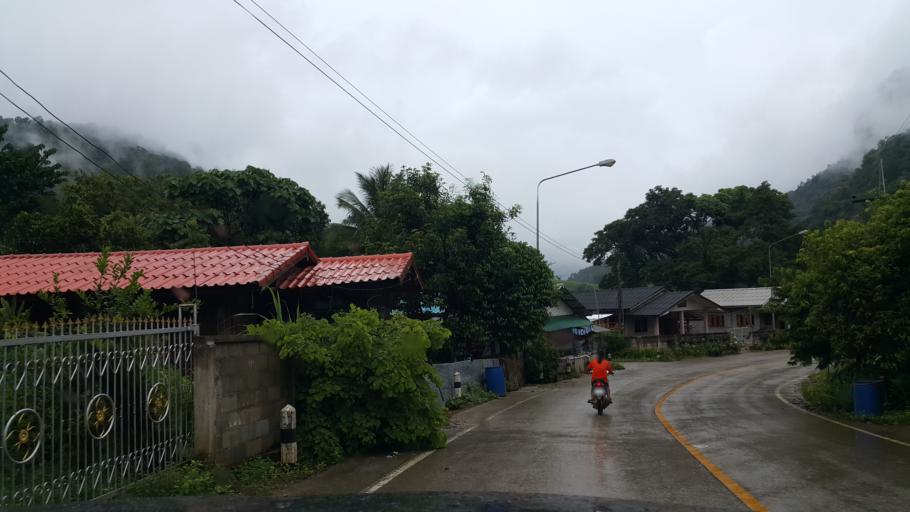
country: TH
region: Phayao
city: Chiang Kham
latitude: 19.5004
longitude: 100.4564
